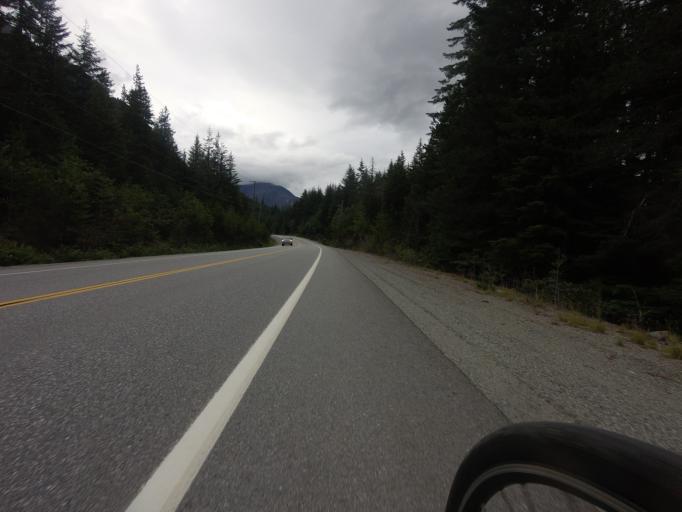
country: CA
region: British Columbia
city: Whistler
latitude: 50.1929
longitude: -122.8775
